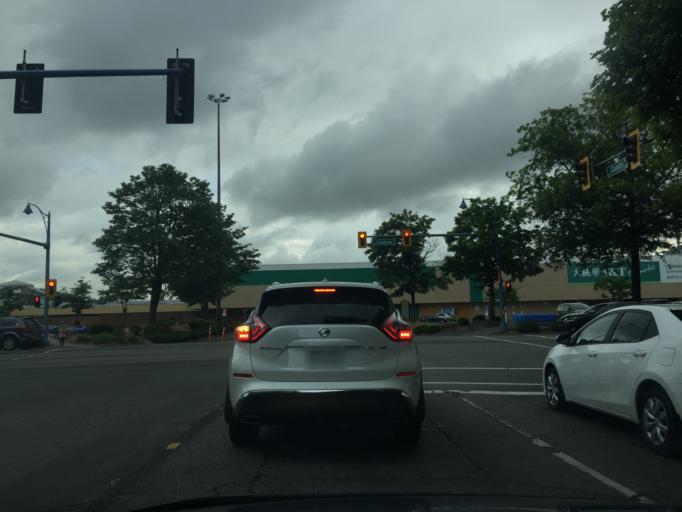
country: CA
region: British Columbia
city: Richmond
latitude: 49.1736
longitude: -123.1315
